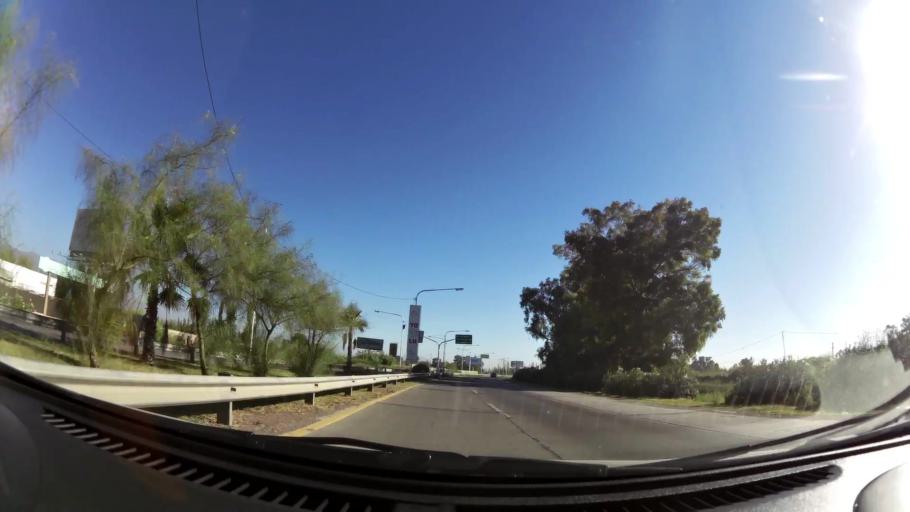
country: AR
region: Mendoza
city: Las Heras
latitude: -32.8328
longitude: -68.8068
